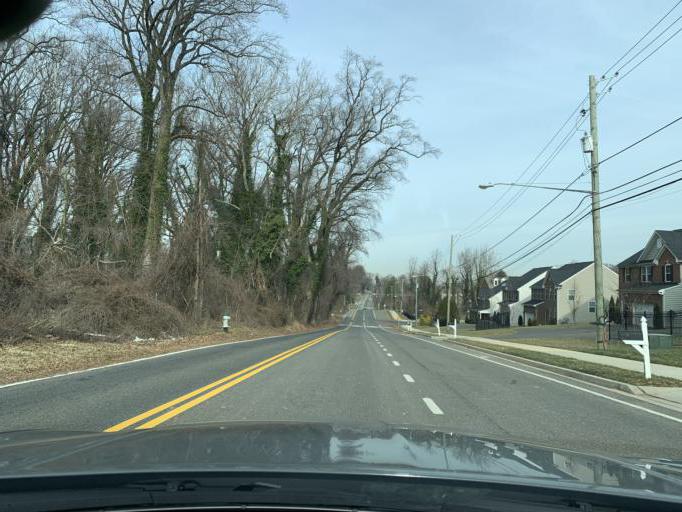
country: US
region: Maryland
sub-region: Prince George's County
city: Walker Mill
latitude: 38.8795
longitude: -76.9021
